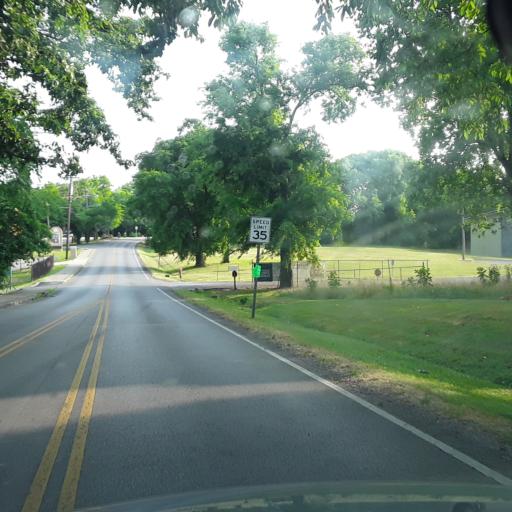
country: US
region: Tennessee
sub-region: Williamson County
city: Brentwood
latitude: 36.0584
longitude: -86.7225
